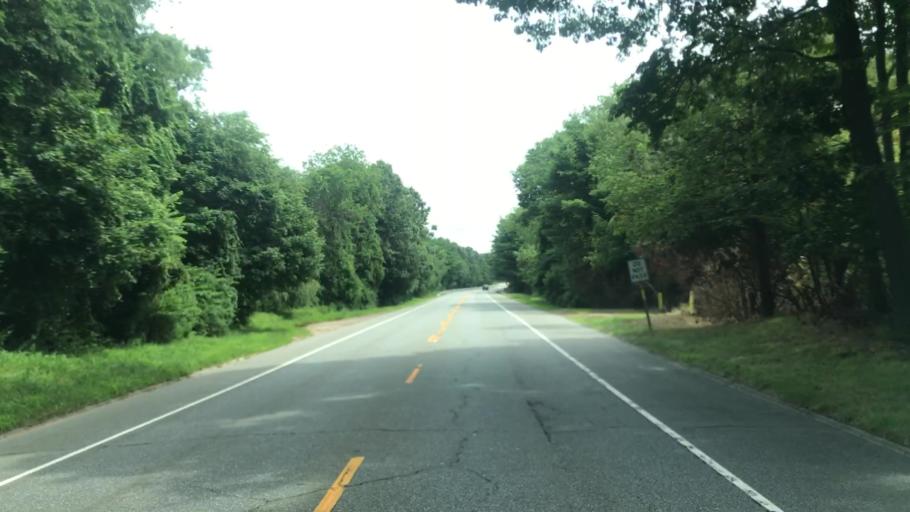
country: US
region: Connecticut
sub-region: Middlesex County
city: Old Saybrook Center
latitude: 41.3091
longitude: -72.3329
